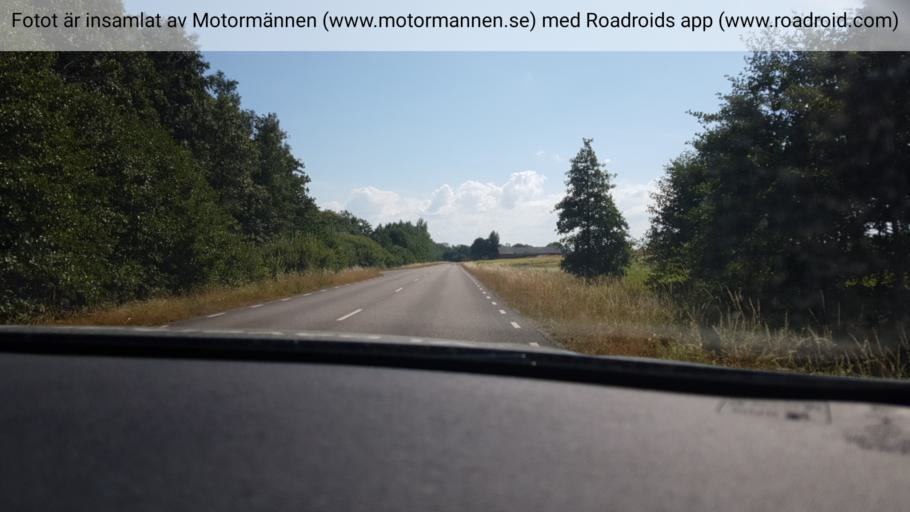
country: SE
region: Vaestra Goetaland
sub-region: Gotene Kommun
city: Kallby
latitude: 58.5886
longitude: 13.3789
